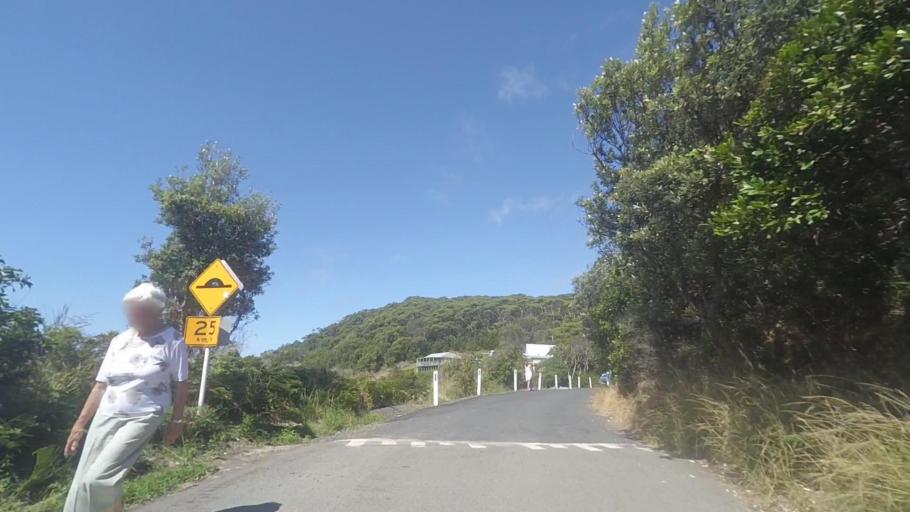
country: AU
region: New South Wales
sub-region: Great Lakes
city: Forster
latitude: -32.4357
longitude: 152.5340
